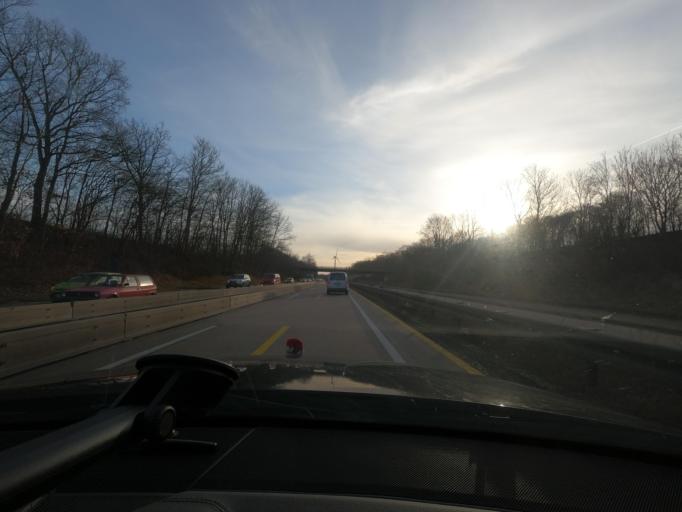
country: DE
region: Lower Saxony
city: Harsum
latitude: 52.2161
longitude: 9.9339
